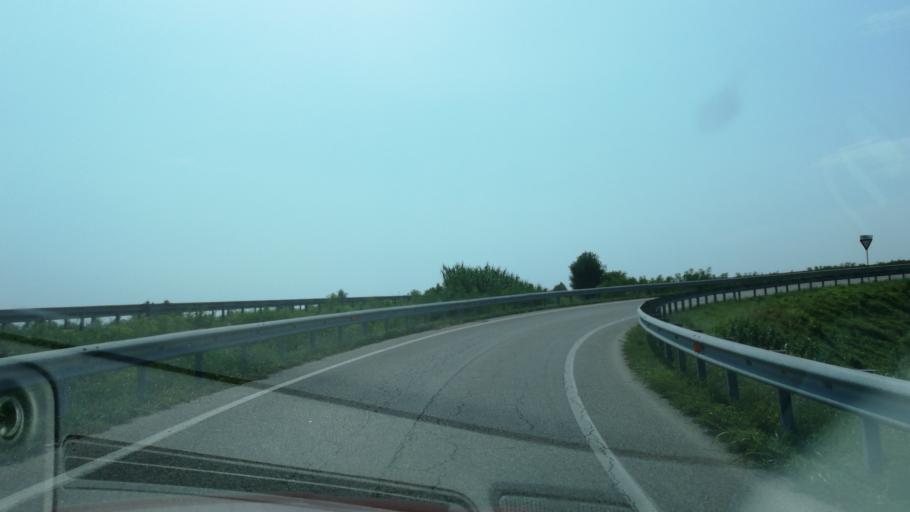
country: IT
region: Friuli Venezia Giulia
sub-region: Provincia di Udine
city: Latisana
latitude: 45.7929
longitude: 13.0261
